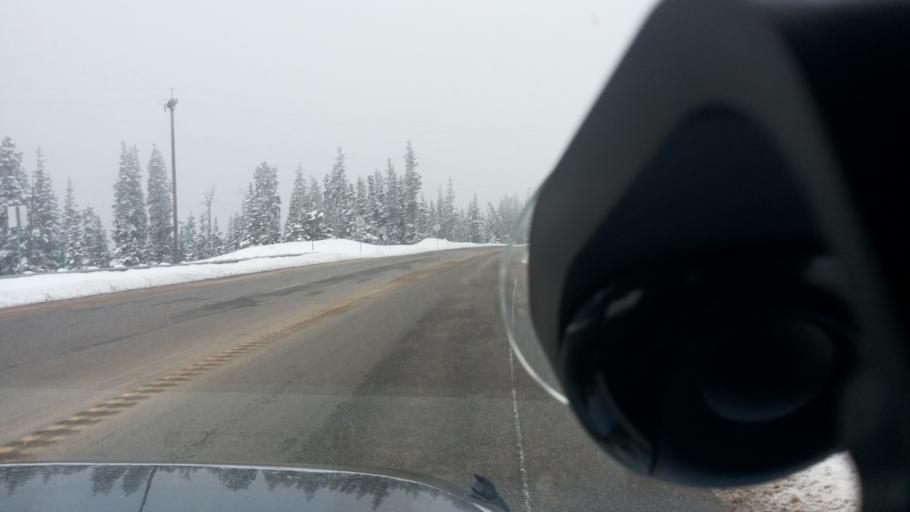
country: US
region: Colorado
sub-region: Clear Creek County
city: Georgetown
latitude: 39.7979
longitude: -105.7775
